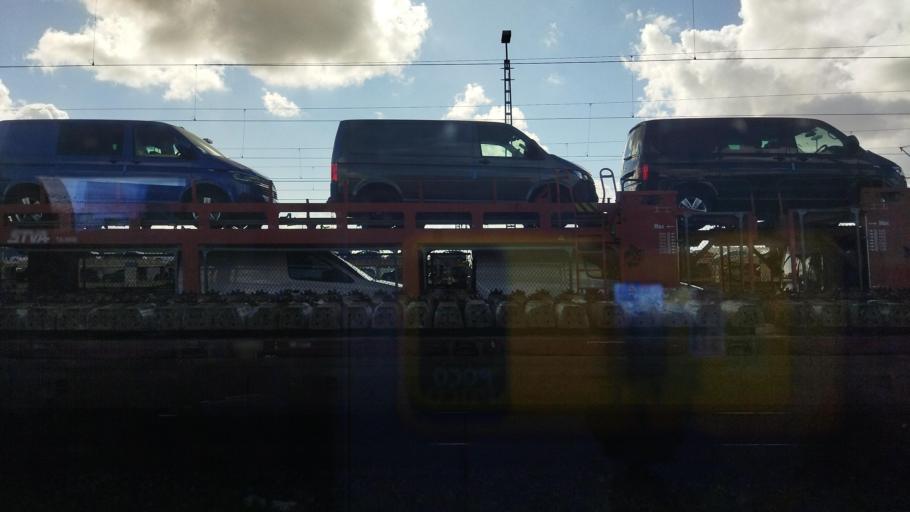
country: DE
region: Lower Saxony
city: Emden
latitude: 53.3595
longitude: 7.2129
